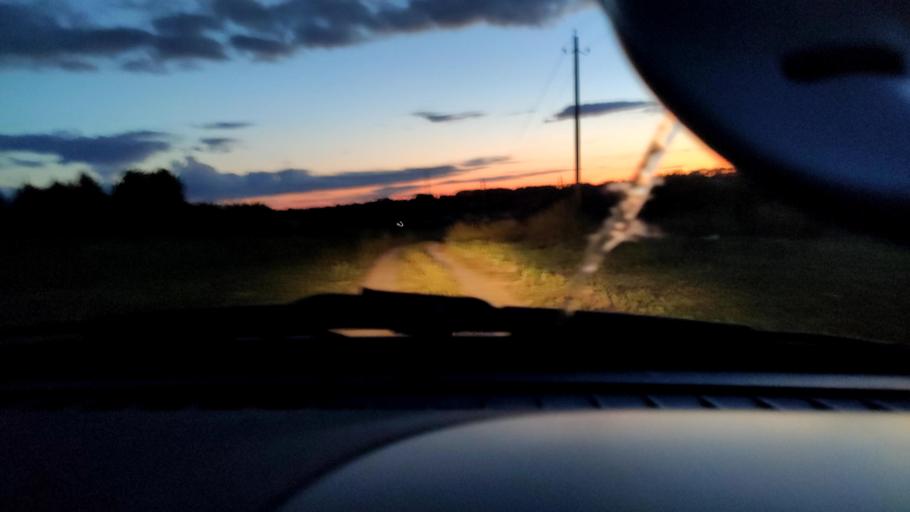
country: RU
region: Perm
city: Froly
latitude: 57.9461
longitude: 56.2539
